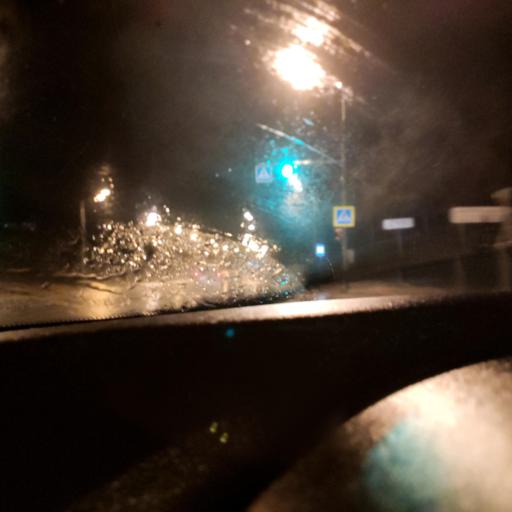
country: RU
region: Samara
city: Petra-Dubrava
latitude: 53.3075
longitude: 50.2371
